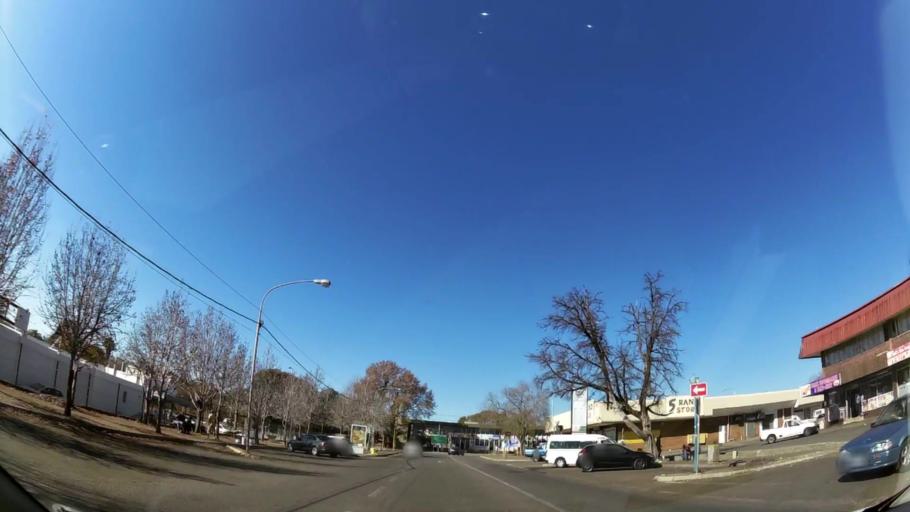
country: ZA
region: Gauteng
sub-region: City of Tshwane Metropolitan Municipality
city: Centurion
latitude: -25.8291
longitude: 28.2047
